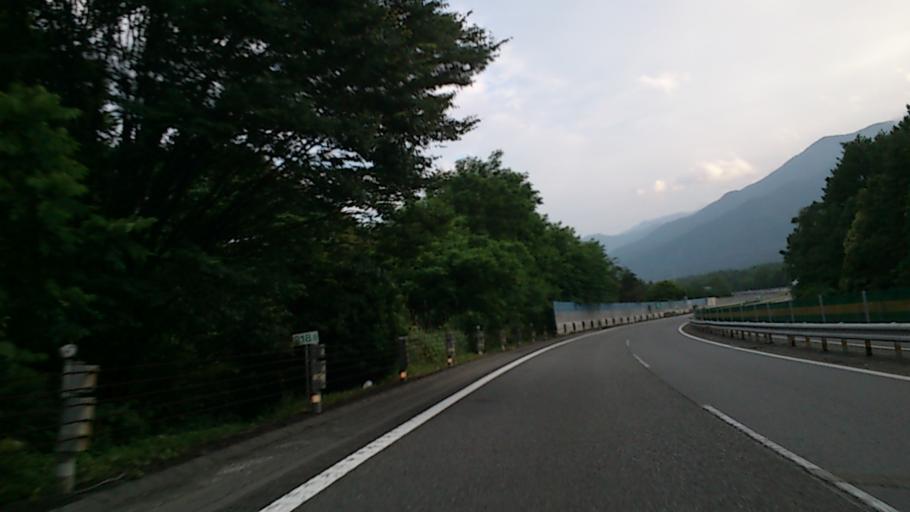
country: JP
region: Nagano
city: Ina
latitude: 35.7566
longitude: 137.9165
